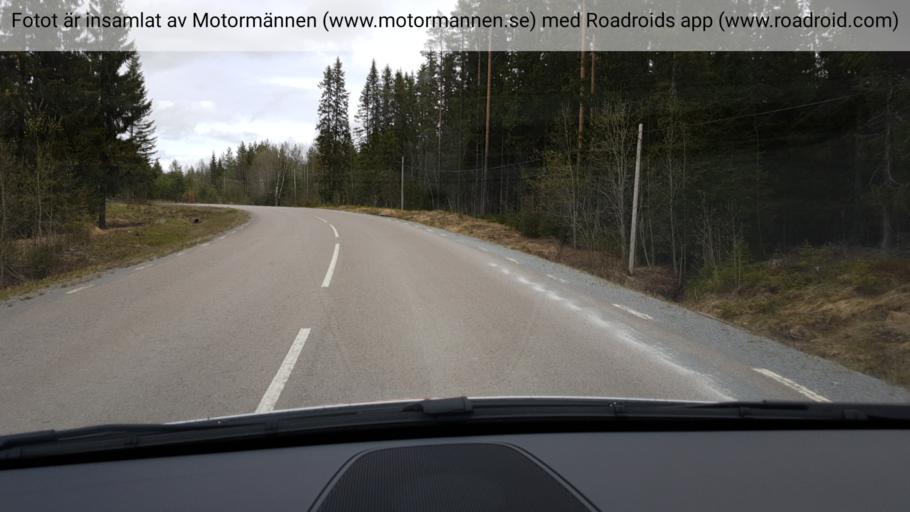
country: SE
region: Jaemtland
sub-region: Bergs Kommun
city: Hoverberg
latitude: 62.6562
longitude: 14.8291
